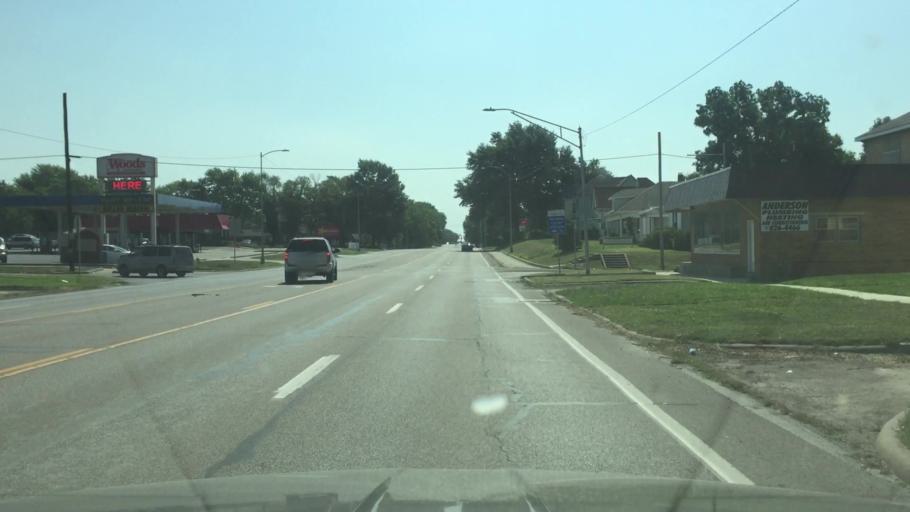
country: US
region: Missouri
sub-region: Pettis County
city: Sedalia
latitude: 38.7038
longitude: -93.2201
